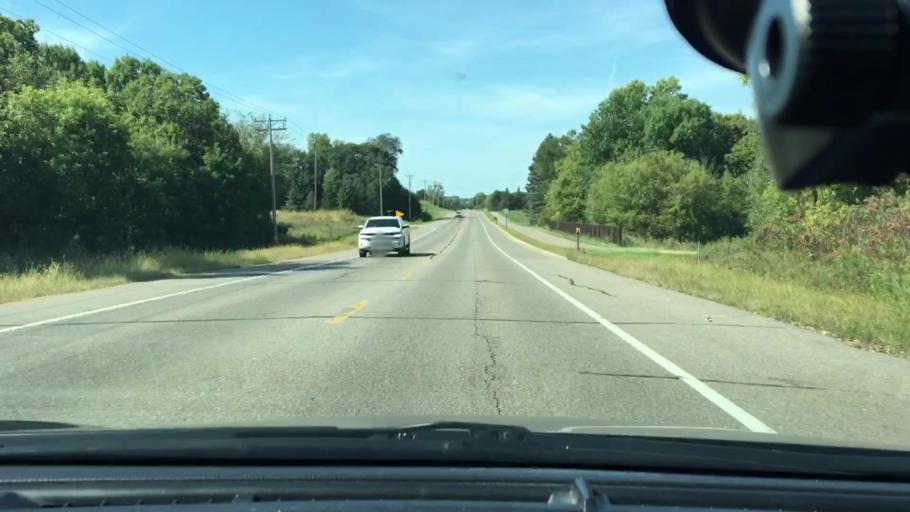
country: US
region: Minnesota
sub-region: Wright County
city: Hanover
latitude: 45.1526
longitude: -93.6440
